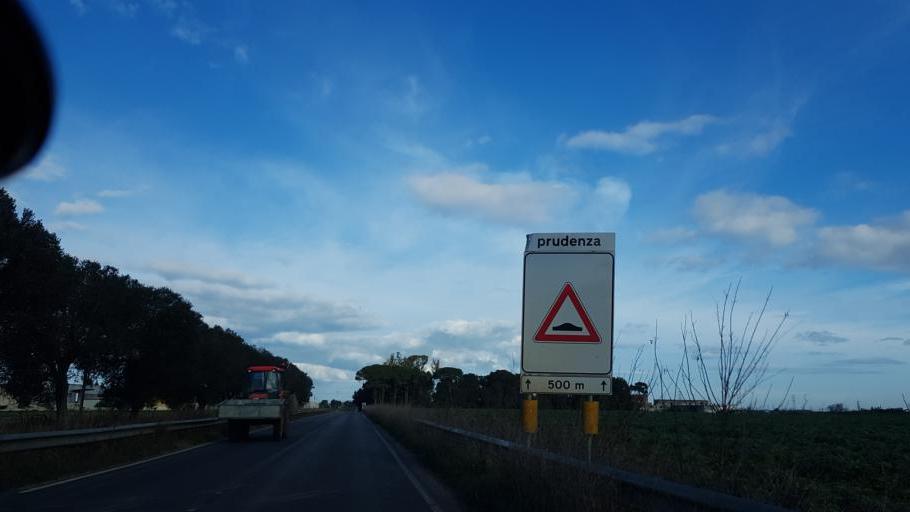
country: IT
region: Apulia
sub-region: Provincia di Brindisi
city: La Rosa
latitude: 40.5832
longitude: 17.9635
